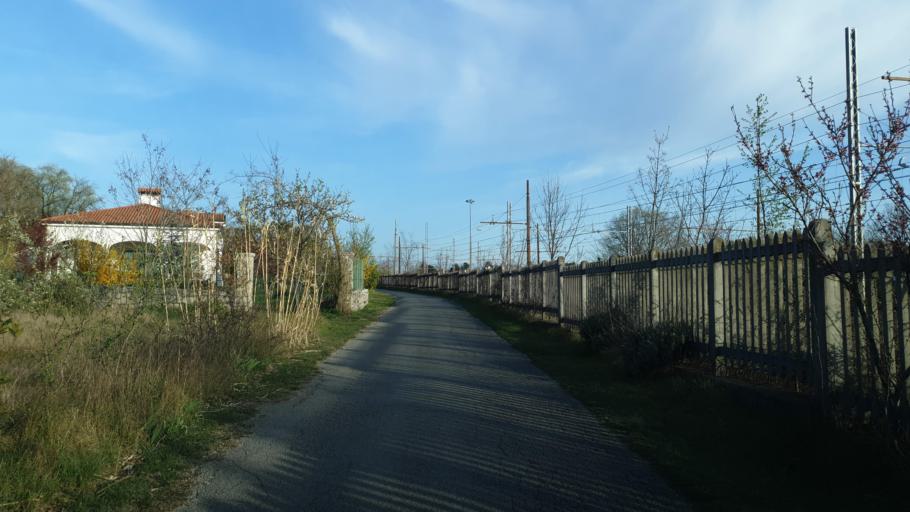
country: IT
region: Friuli Venezia Giulia
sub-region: Provincia di Trieste
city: Sgonico
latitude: 45.7171
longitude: 13.7526
